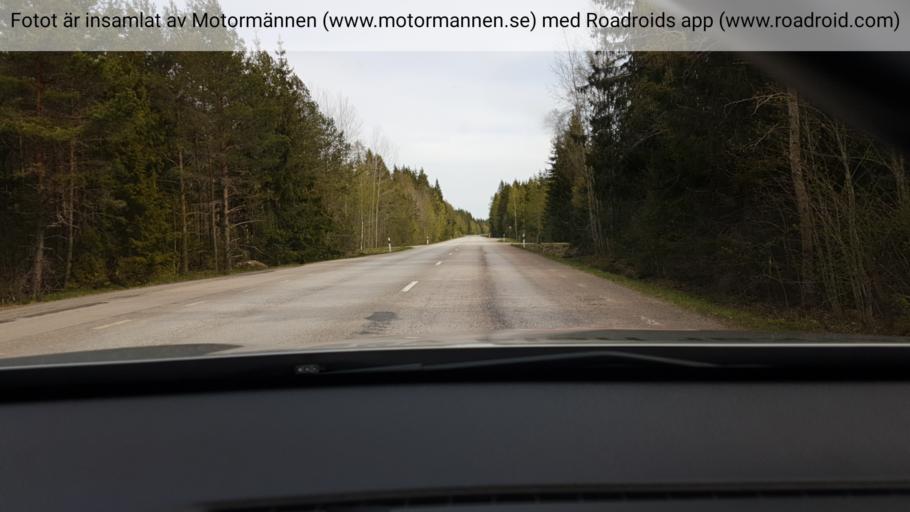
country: SE
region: Uppsala
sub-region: Tierps Kommun
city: Orbyhus
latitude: 60.2112
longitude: 17.7684
